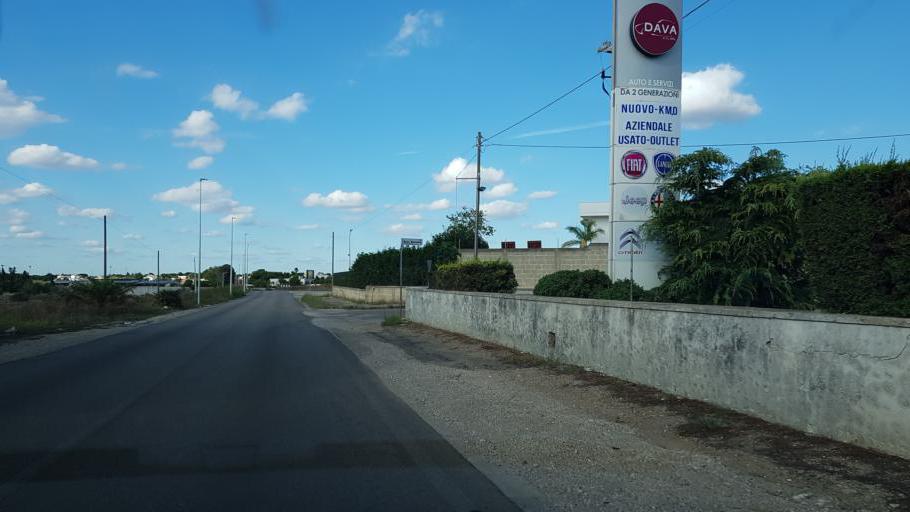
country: IT
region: Apulia
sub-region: Provincia di Lecce
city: Nardo
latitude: 40.1461
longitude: 18.0186
